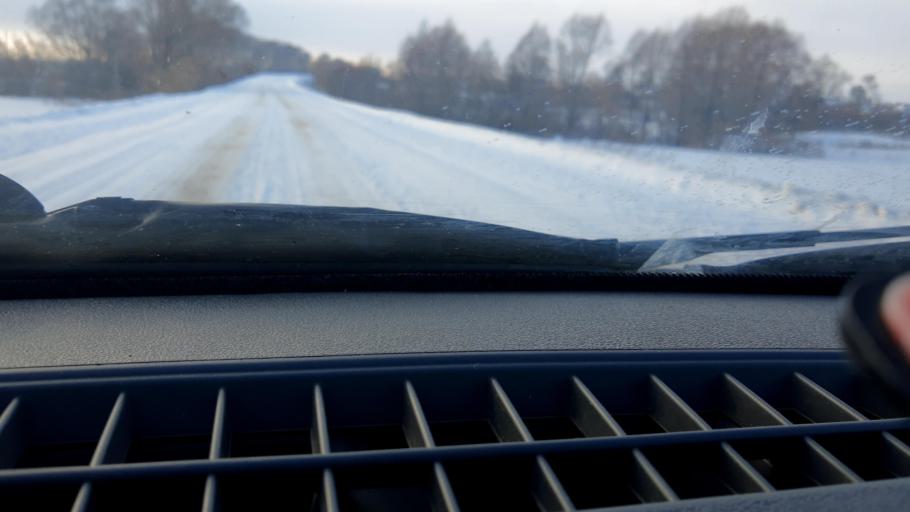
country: RU
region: Bashkortostan
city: Kushnarenkovo
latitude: 55.1134
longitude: 55.5527
